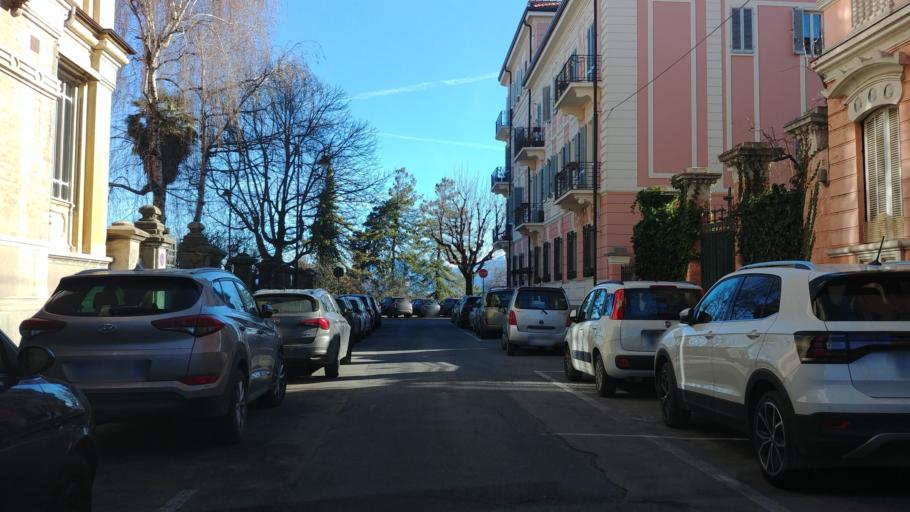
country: IT
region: Piedmont
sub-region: Provincia di Cuneo
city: Cuneo
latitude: 44.3867
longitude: 7.5491
